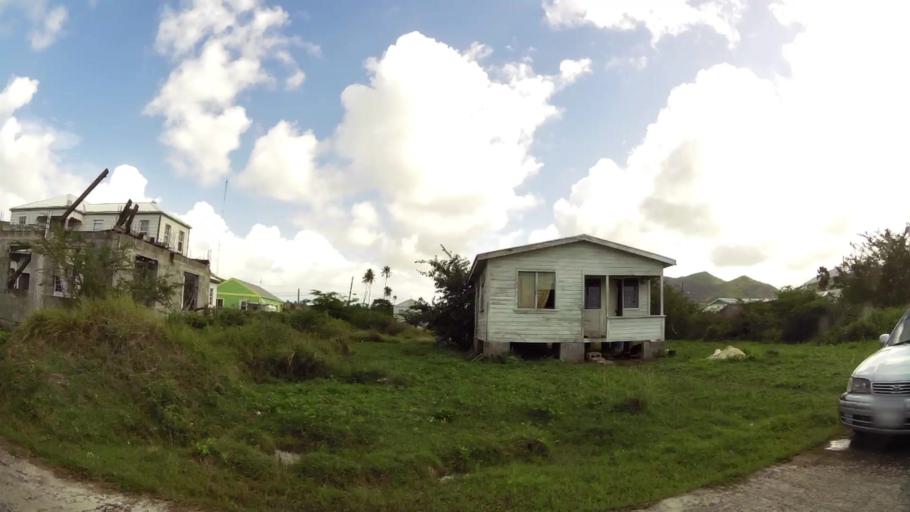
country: AG
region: Saint Mary
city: Bolands
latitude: 17.0755
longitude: -61.8753
